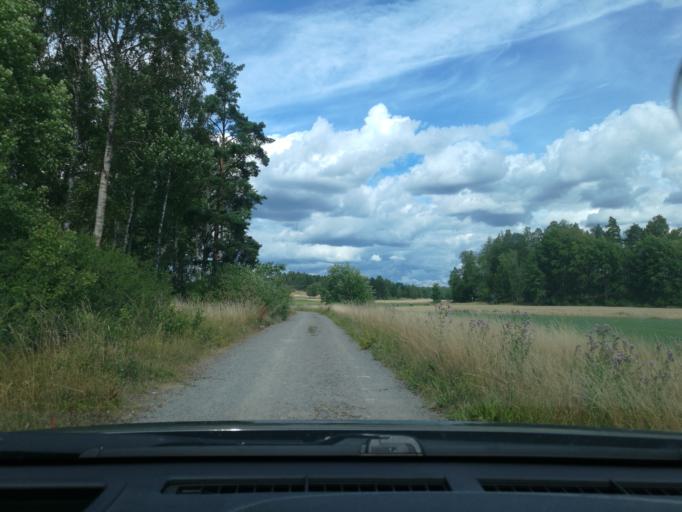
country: SE
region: Stockholm
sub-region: Sigtuna Kommun
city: Marsta
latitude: 59.6138
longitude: 17.8002
